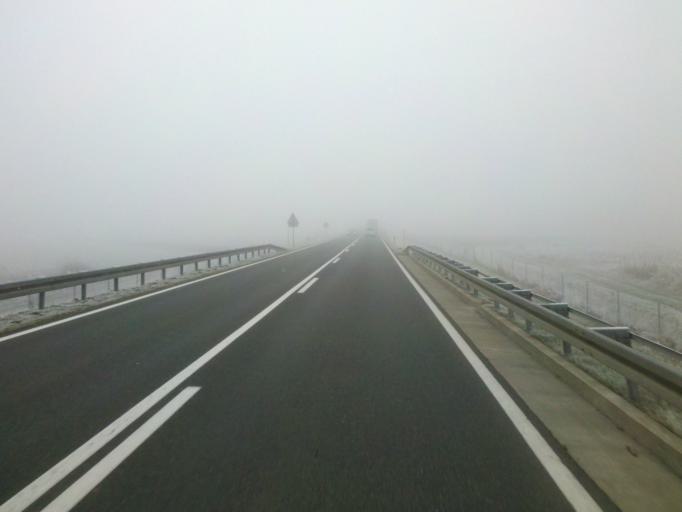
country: HR
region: Varazdinska
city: Jalkovec
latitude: 46.2822
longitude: 16.3093
